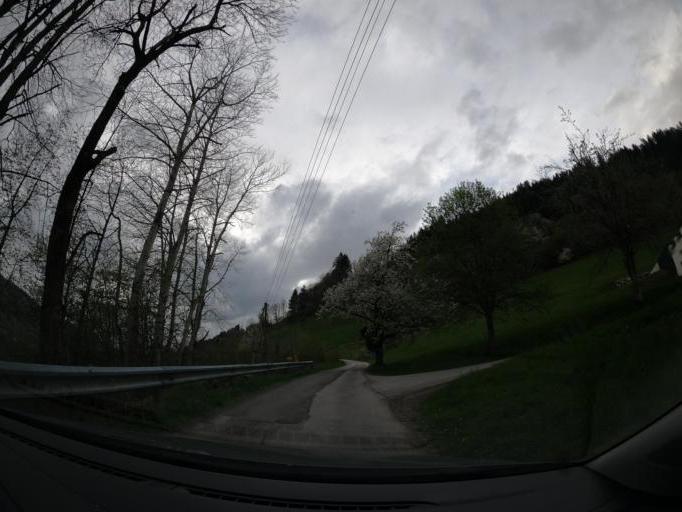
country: AT
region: Salzburg
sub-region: Politischer Bezirk Zell am See
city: Lend
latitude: 47.3017
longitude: 13.0686
